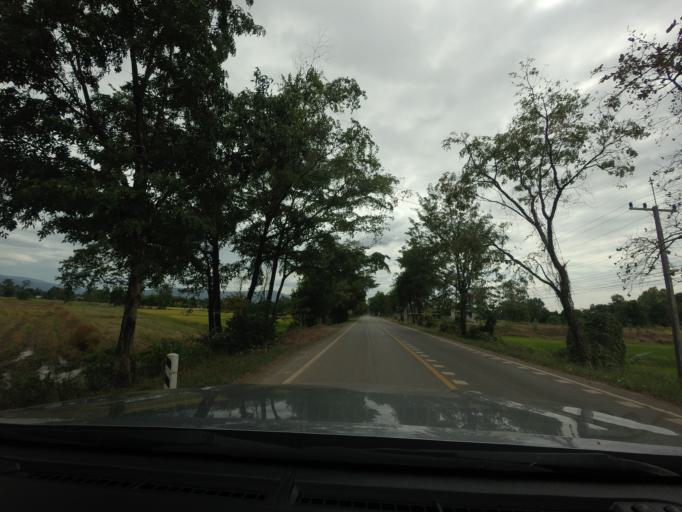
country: TH
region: Phitsanulok
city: Noen Maprang
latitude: 16.6857
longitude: 100.5999
